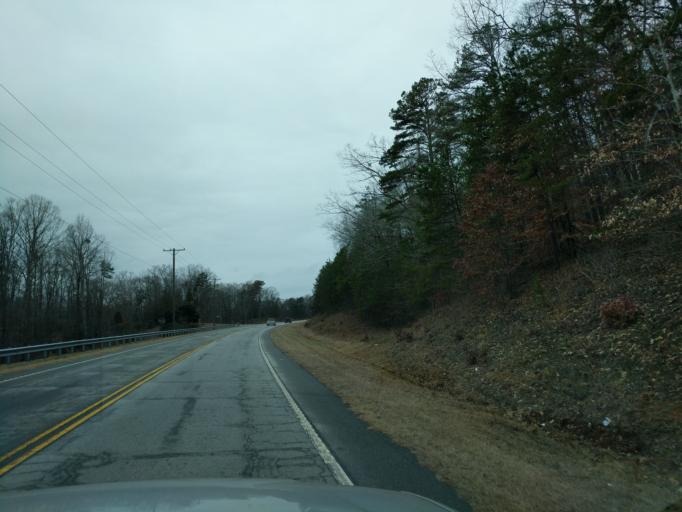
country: US
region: South Carolina
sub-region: Pickens County
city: Pickens
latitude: 34.9150
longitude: -82.9157
